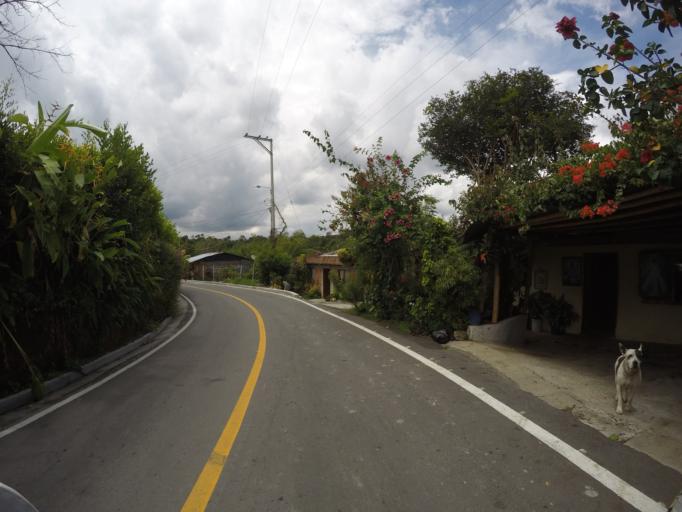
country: CO
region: Quindio
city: Quimbaya
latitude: 4.6129
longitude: -75.7518
